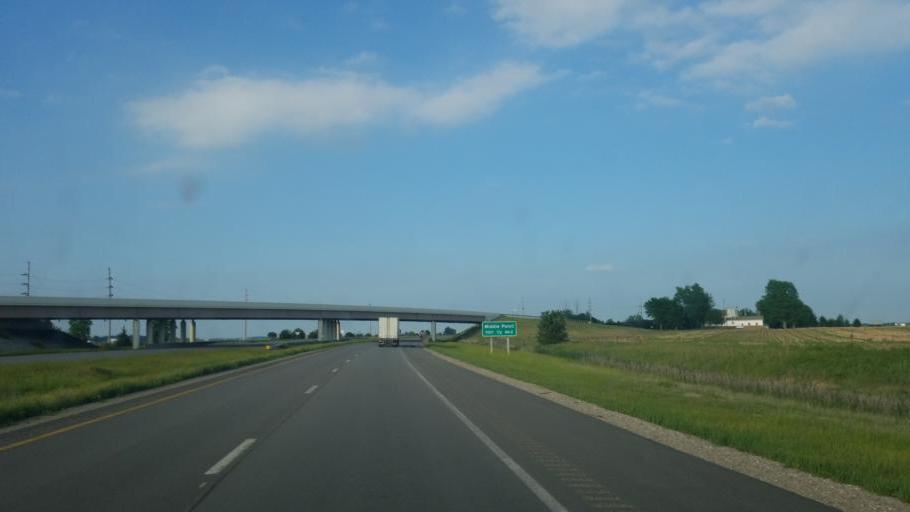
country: US
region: Ohio
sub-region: Allen County
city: Delphos
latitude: 40.8713
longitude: -84.4502
